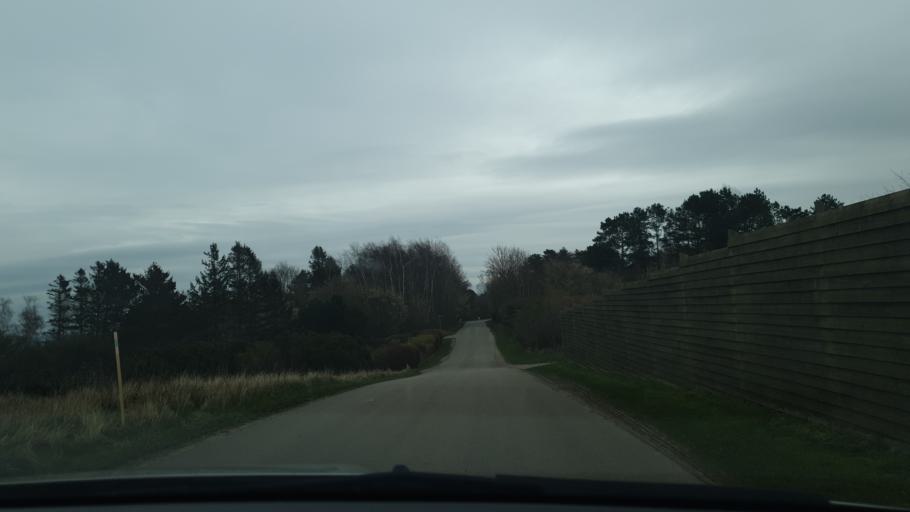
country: DK
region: Zealand
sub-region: Odsherred Kommune
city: Asnaes
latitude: 55.8403
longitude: 11.4453
